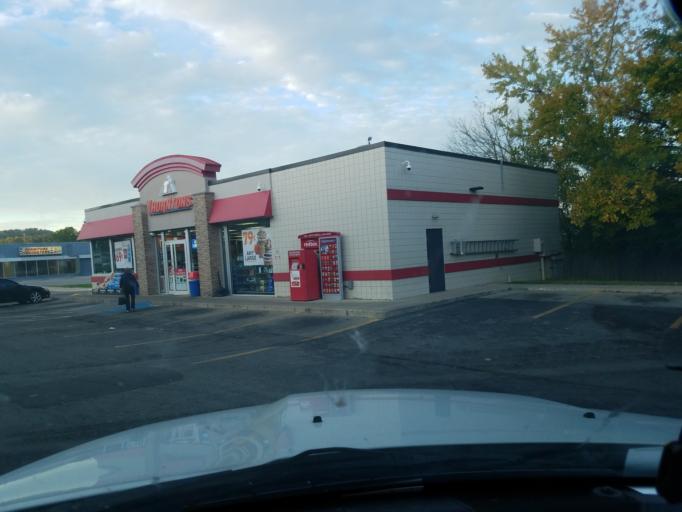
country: US
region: Indiana
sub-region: Floyd County
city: New Albany
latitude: 38.3077
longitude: -85.8420
